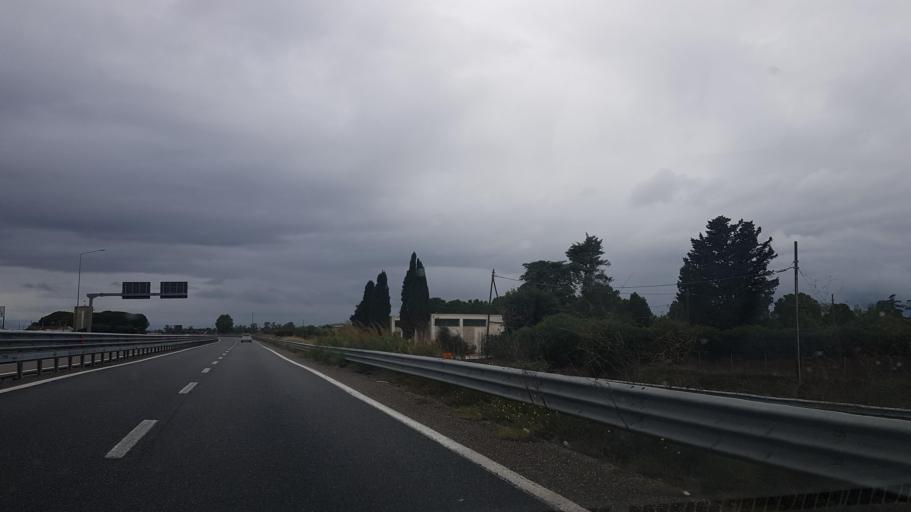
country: IT
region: Apulia
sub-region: Provincia di Taranto
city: Marina di Ginosa
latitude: 40.4151
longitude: 16.8191
